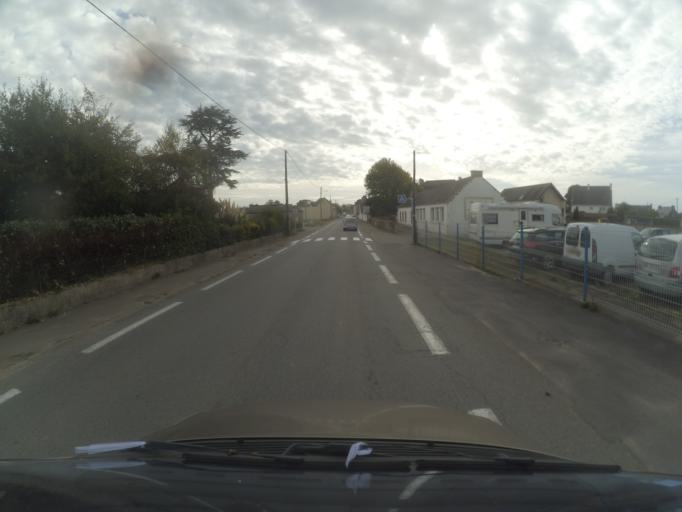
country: FR
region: Brittany
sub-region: Departement du Morbihan
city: Erdeven
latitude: 47.6442
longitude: -3.1571
